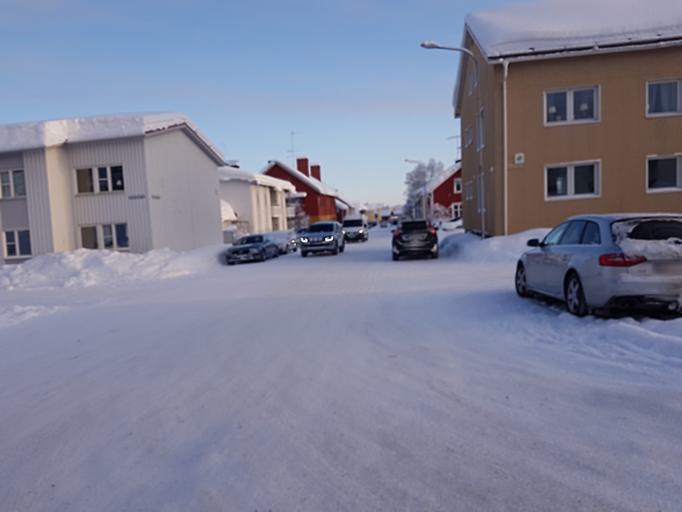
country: SE
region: Norrbotten
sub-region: Jokkmokks Kommun
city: Jokkmokk
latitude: 66.6079
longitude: 19.8241
